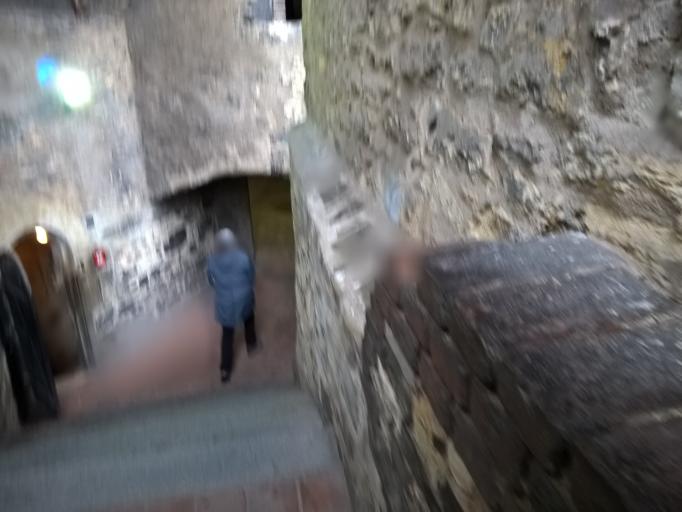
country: CZ
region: Praha
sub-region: Praha 1
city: Mala Strana
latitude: 50.0922
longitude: 14.4050
